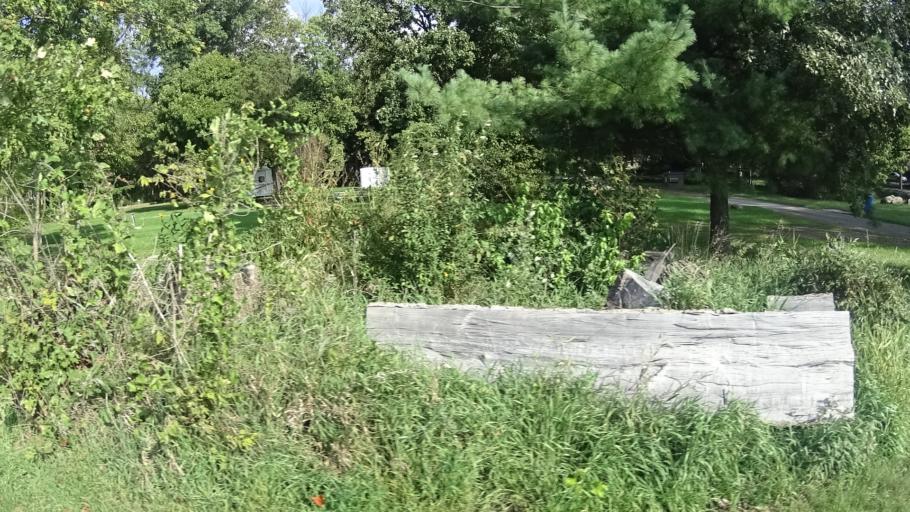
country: US
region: Indiana
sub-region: Madison County
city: Ingalls
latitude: 40.0023
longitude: -85.8514
